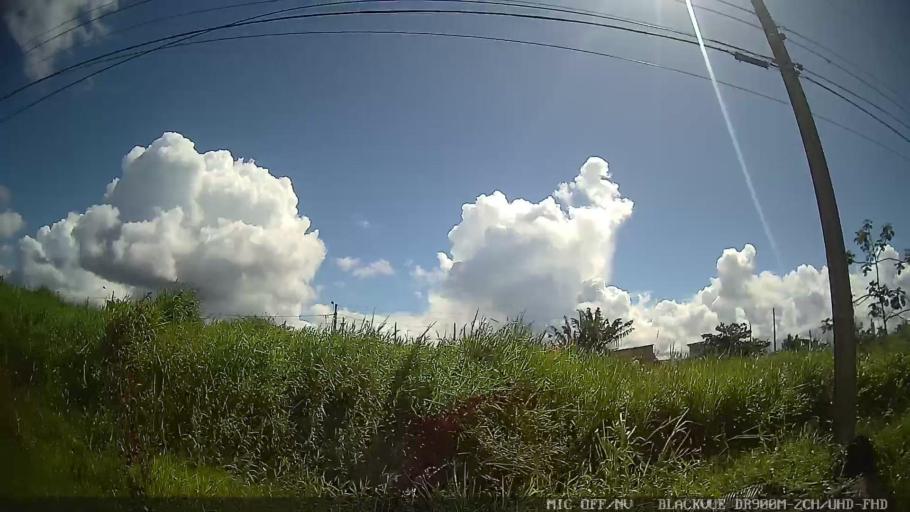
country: BR
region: Sao Paulo
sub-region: Itanhaem
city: Itanhaem
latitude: -24.2200
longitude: -46.8618
